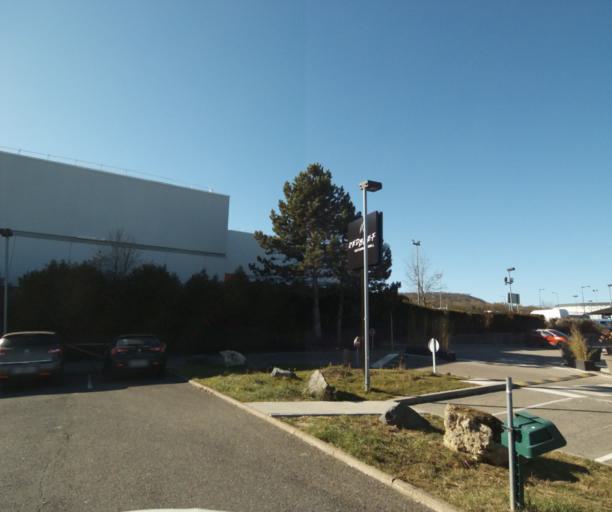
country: FR
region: Lorraine
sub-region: Departement de Meurthe-et-Moselle
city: Vandoeuvre-les-Nancy
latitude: 48.6425
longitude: 6.1844
